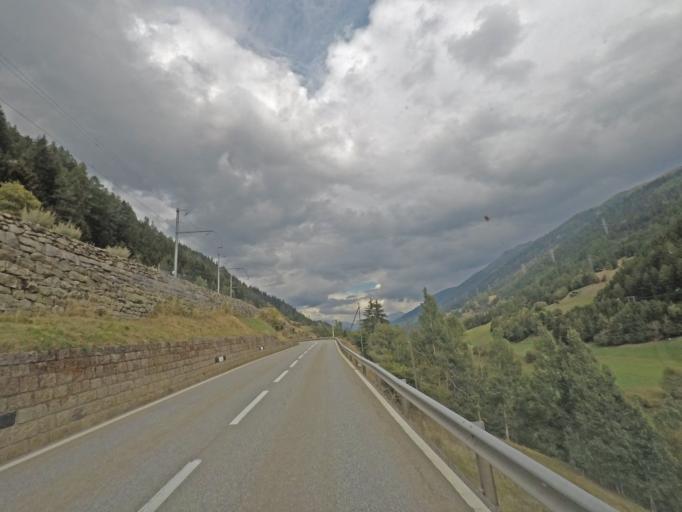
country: CH
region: Valais
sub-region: Goms District
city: Fiesch
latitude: 46.4283
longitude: 8.1785
